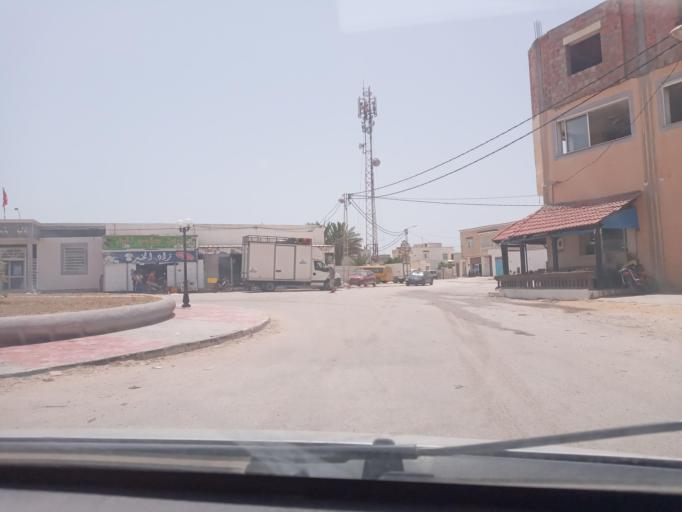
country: TN
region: Nabul
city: El Haouaria
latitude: 37.0116
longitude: 10.9536
